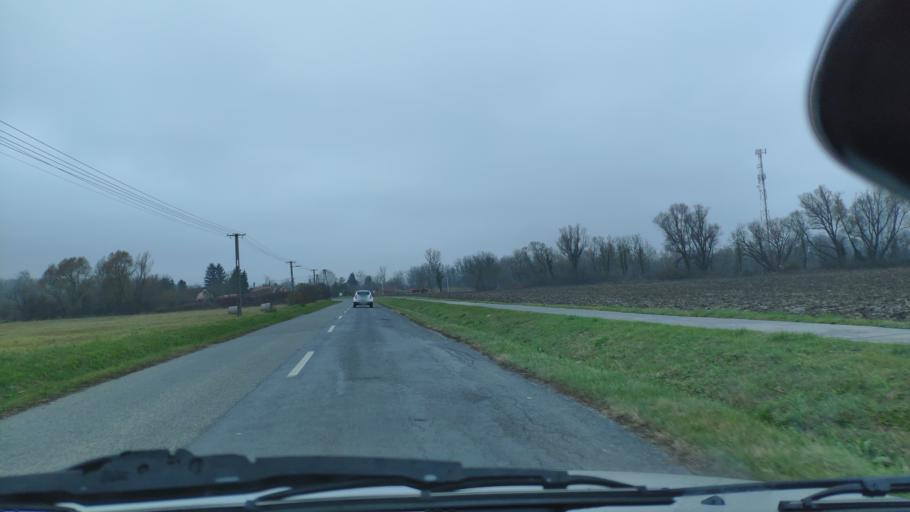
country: HU
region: Zala
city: Zalakomar
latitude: 46.5549
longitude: 17.1391
